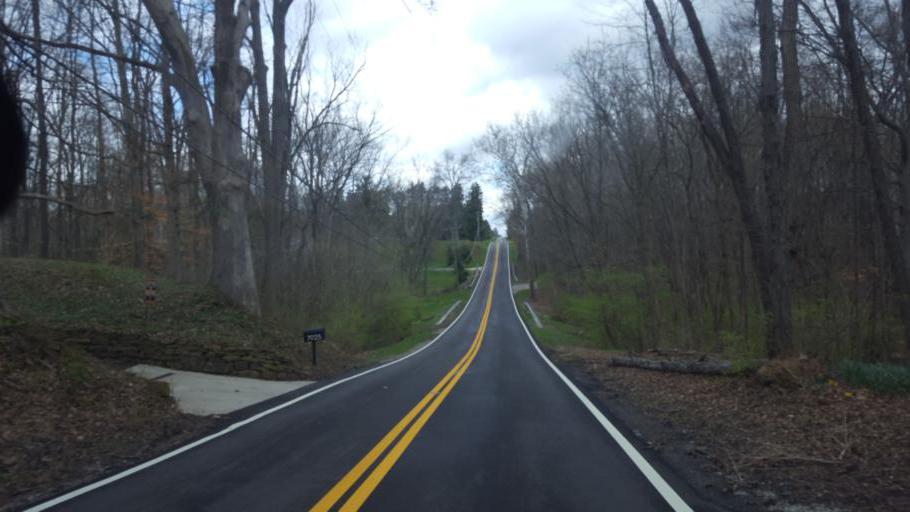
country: US
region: Ohio
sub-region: Franklin County
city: New Albany
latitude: 40.1184
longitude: -82.8590
